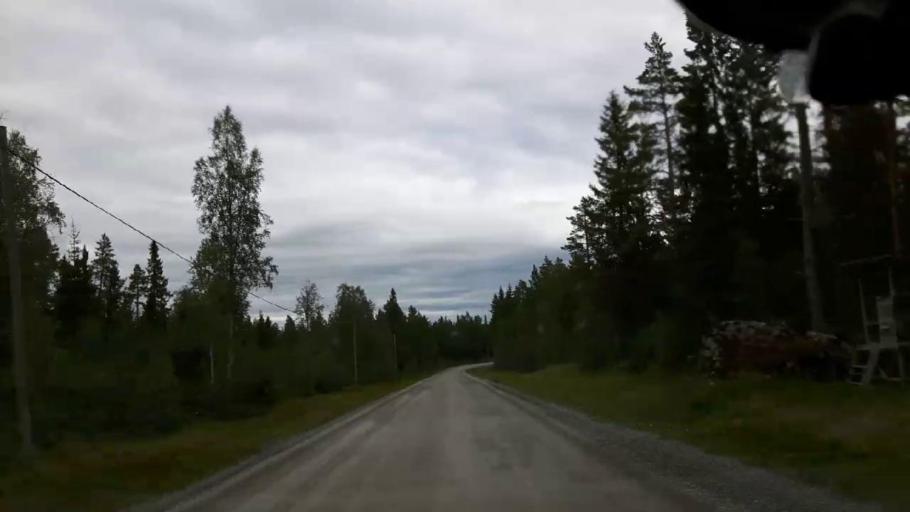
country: SE
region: Jaemtland
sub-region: OEstersunds Kommun
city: Brunflo
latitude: 63.0937
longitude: 14.9014
